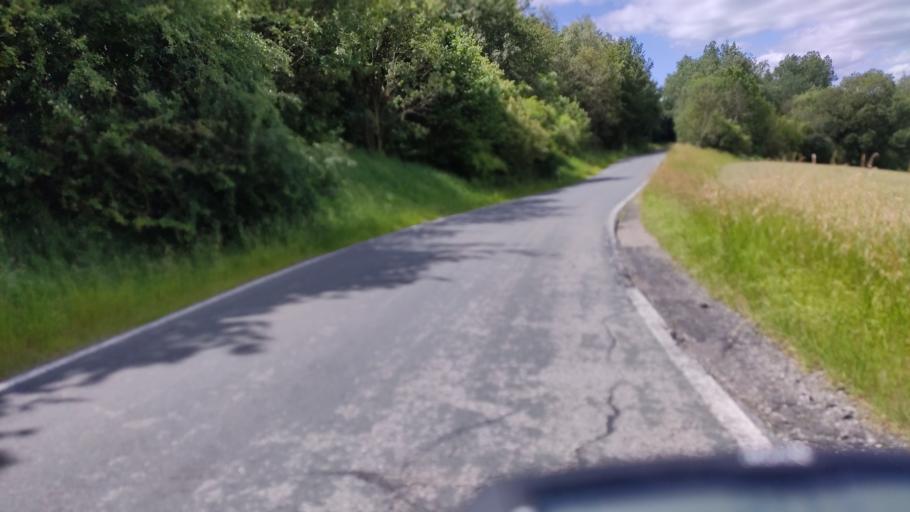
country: DE
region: Thuringia
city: Wurzbach
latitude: 50.4735
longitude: 11.5833
